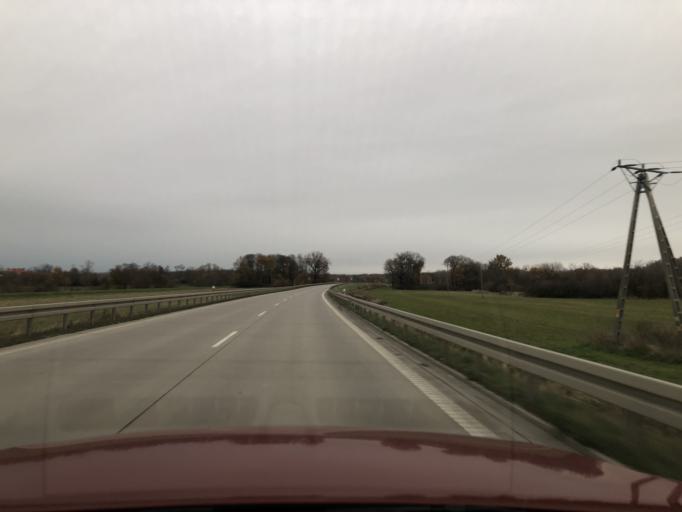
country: PL
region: Lower Silesian Voivodeship
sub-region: Powiat swidnicki
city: Zarow
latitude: 50.9500
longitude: 16.4852
